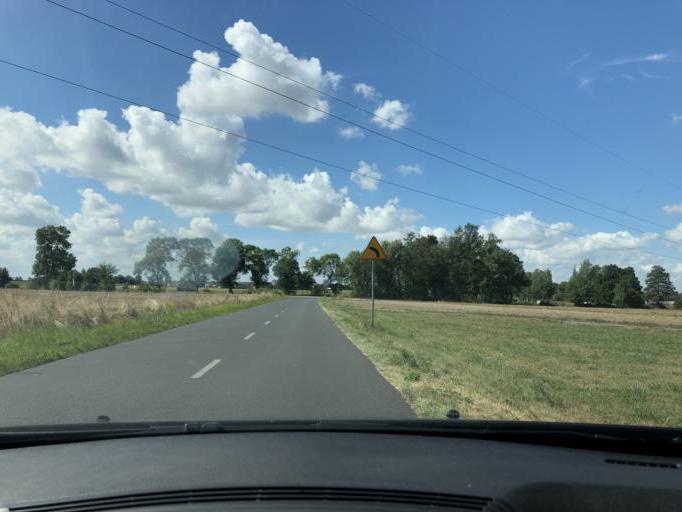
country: PL
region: Lodz Voivodeship
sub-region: Powiat wieruszowski
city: Czastary
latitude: 51.2432
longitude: 18.3668
